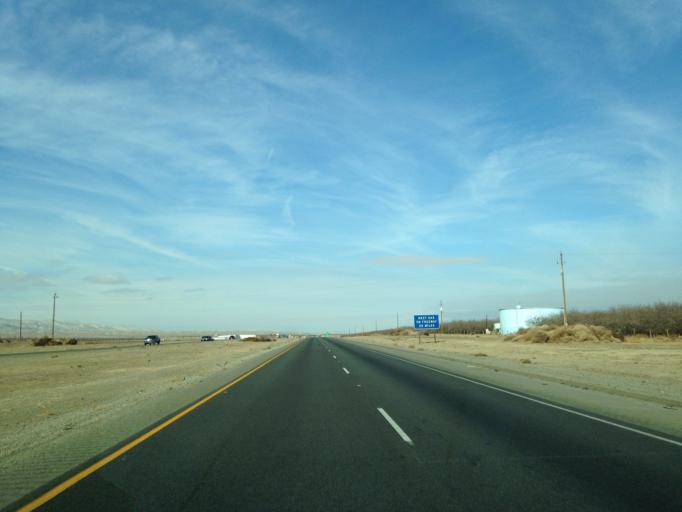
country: US
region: California
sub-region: Fresno County
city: San Joaquin
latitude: 36.4203
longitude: -120.3802
